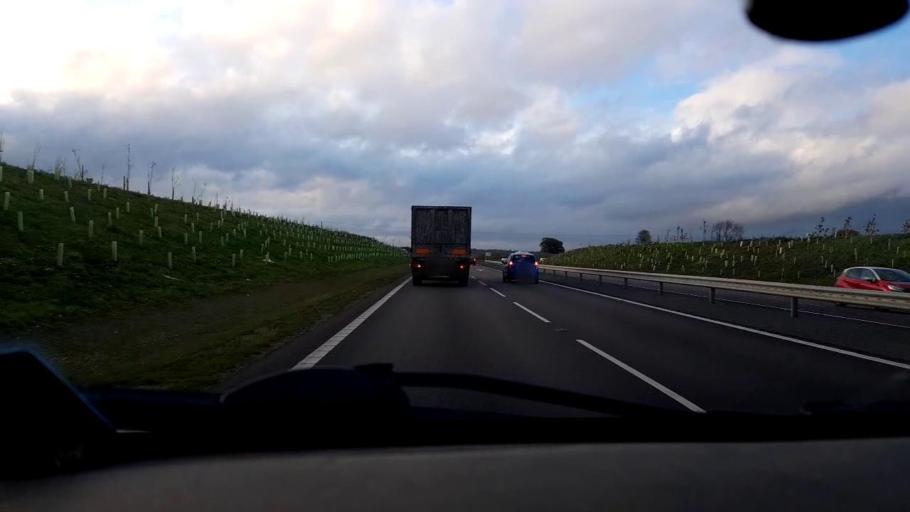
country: GB
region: England
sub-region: Norfolk
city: Horsford
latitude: 52.6853
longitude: 1.2448
